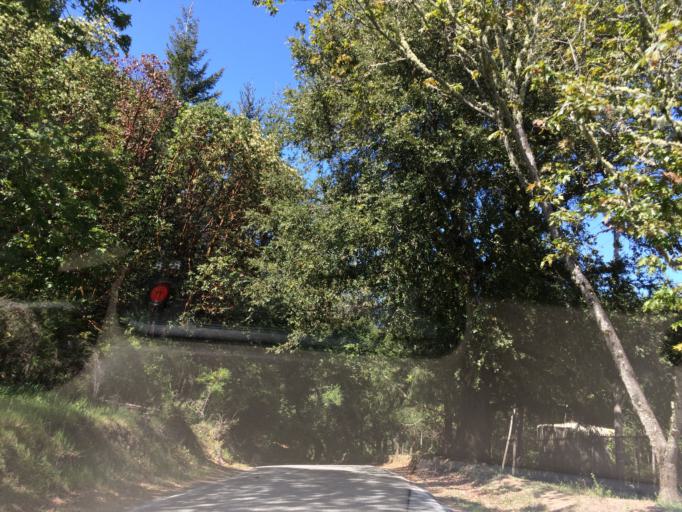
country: US
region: California
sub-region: Santa Clara County
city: Monte Sereno
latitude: 37.1933
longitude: -122.0372
